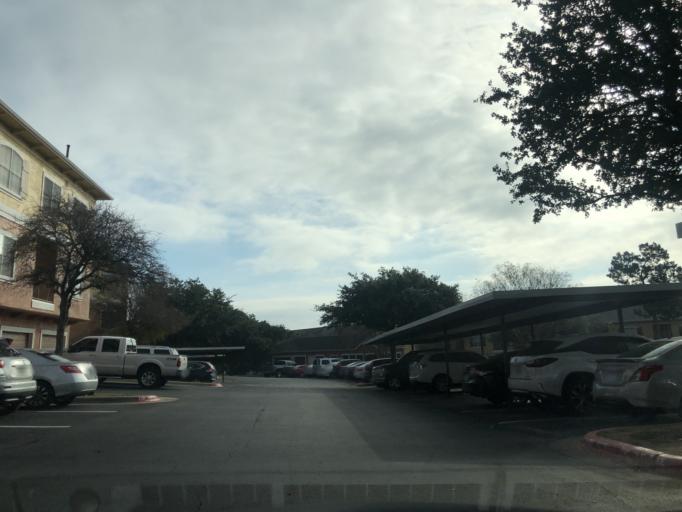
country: US
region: Texas
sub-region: Travis County
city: Wells Branch
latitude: 30.4283
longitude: -97.6974
